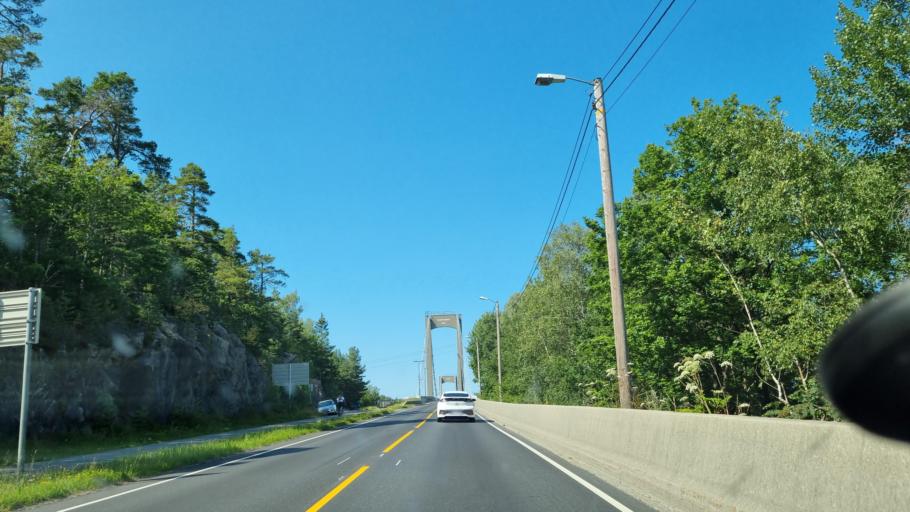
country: NO
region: Aust-Agder
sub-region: Arendal
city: Arendal
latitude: 58.4681
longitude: 8.8246
